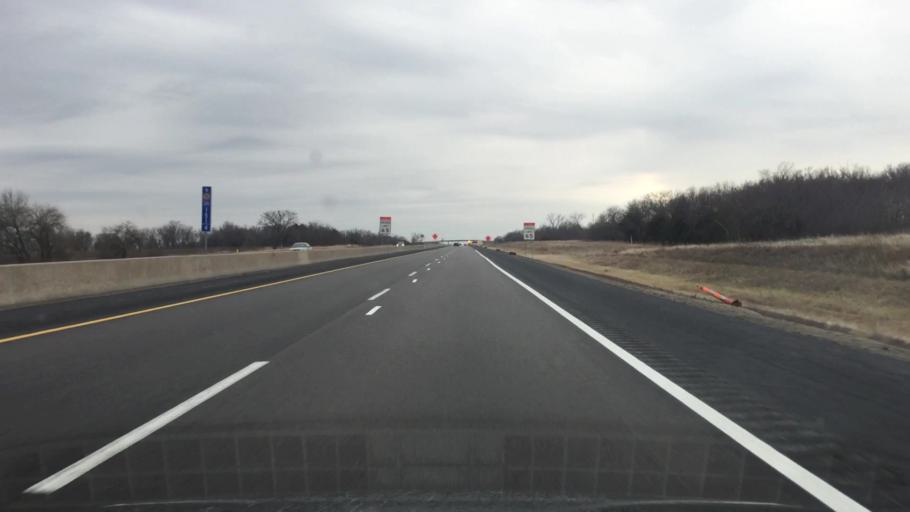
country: US
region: Kansas
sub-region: Osage County
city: Osage City
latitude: 38.7056
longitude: -95.9858
